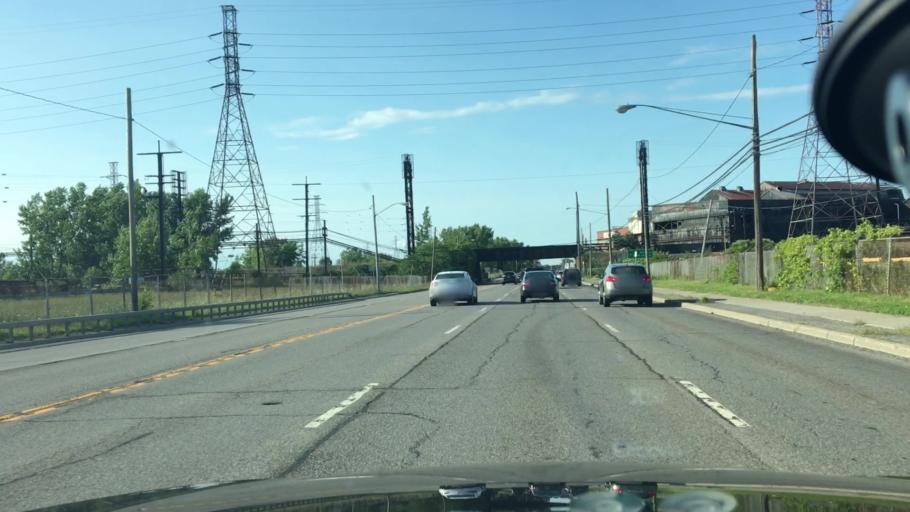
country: US
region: New York
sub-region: Erie County
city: Blasdell
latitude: 42.8026
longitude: -78.8464
